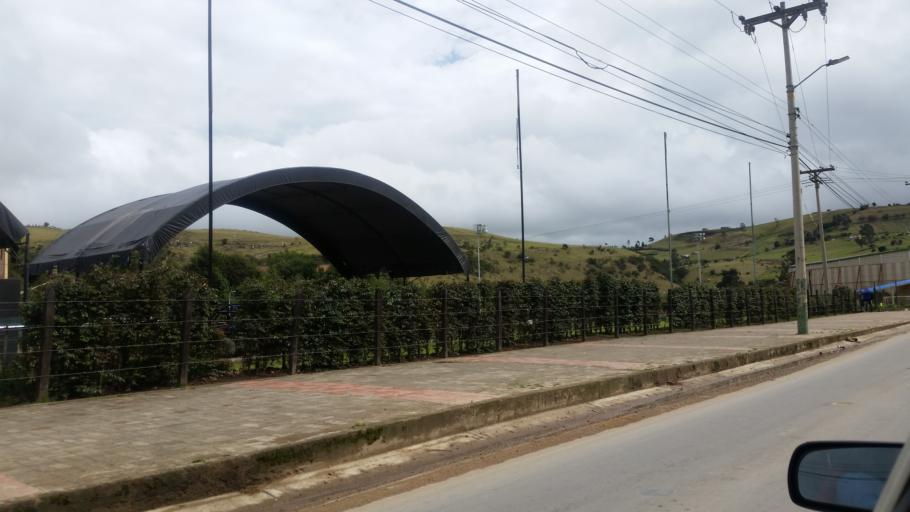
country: CO
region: Cundinamarca
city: La Calera
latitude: 4.7237
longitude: -73.9636
